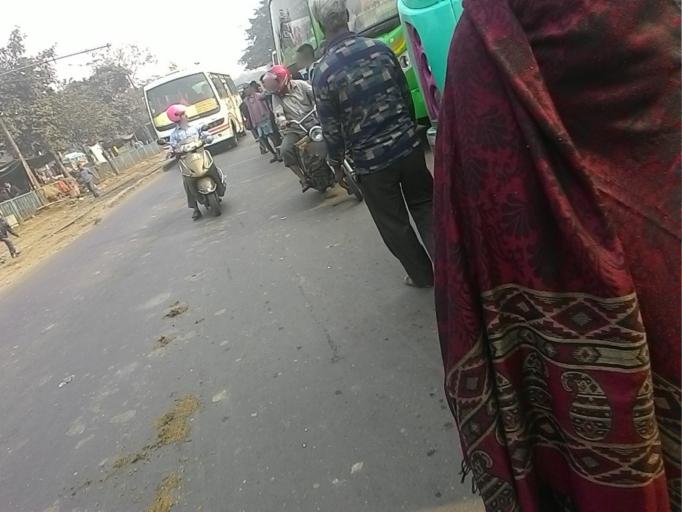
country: IN
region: West Bengal
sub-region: Kolkata
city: Bara Bazar
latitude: 22.5614
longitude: 88.3494
